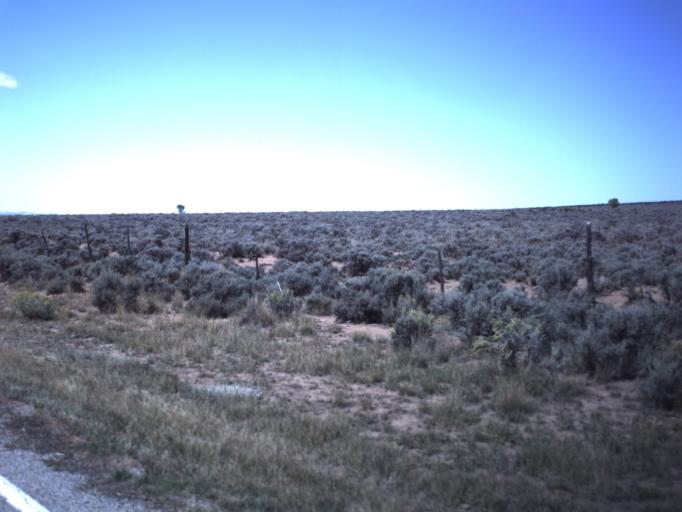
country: US
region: Utah
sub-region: Grand County
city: Moab
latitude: 38.3098
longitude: -109.2642
